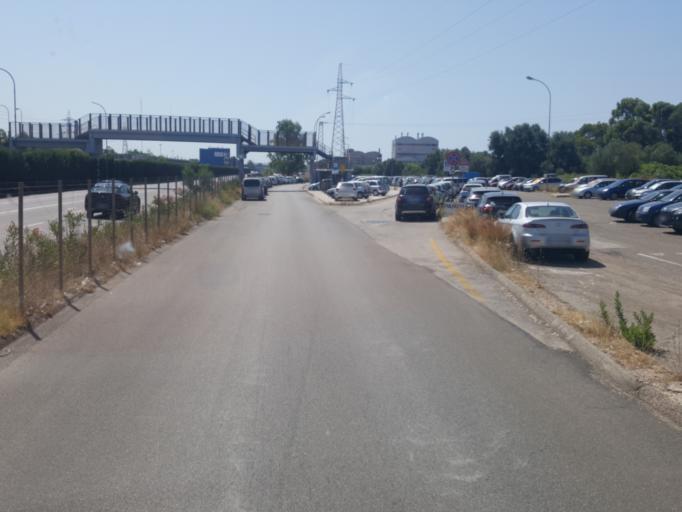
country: IT
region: Apulia
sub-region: Provincia di Taranto
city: Statte
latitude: 40.5049
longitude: 17.1969
